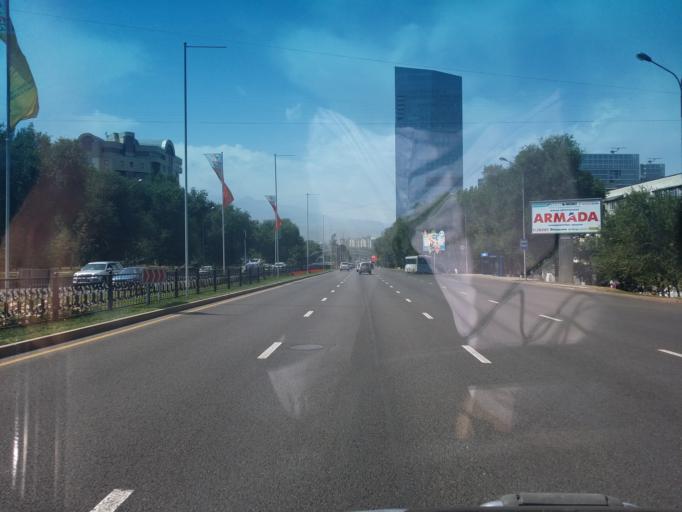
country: KZ
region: Almaty Qalasy
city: Almaty
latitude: 43.2220
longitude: 76.9344
